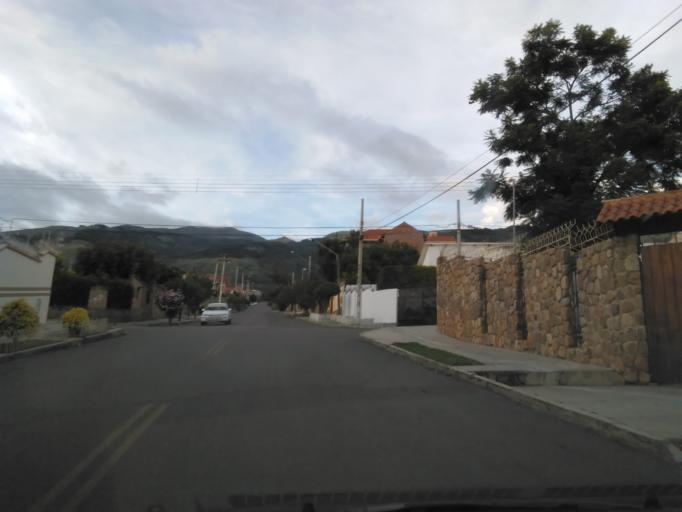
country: BO
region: Cochabamba
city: Cochabamba
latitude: -17.3608
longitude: -66.1562
